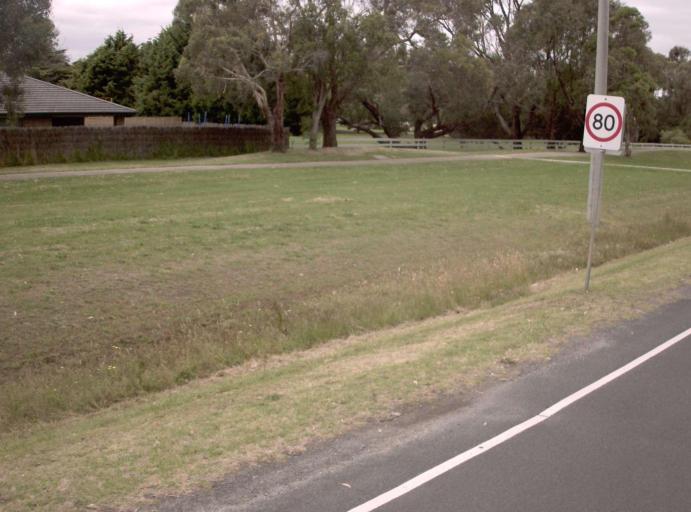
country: AU
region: Victoria
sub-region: Mornington Peninsula
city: Mount Martha
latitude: -38.2543
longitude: 145.0361
